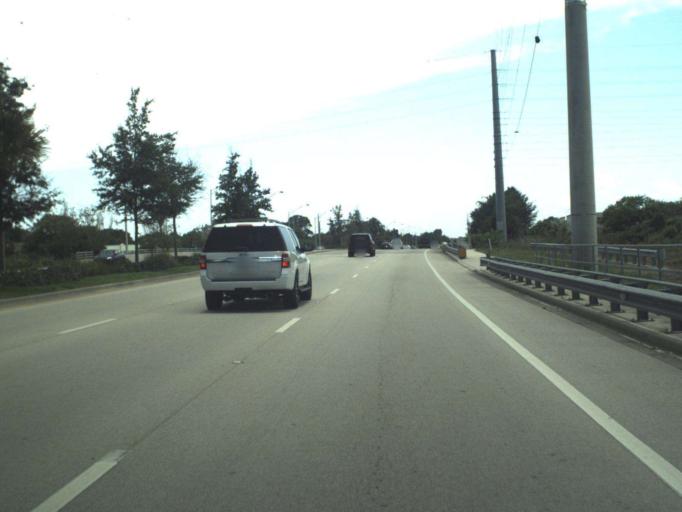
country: US
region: Florida
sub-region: Indian River County
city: Florida Ridge
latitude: 27.6063
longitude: -80.3828
